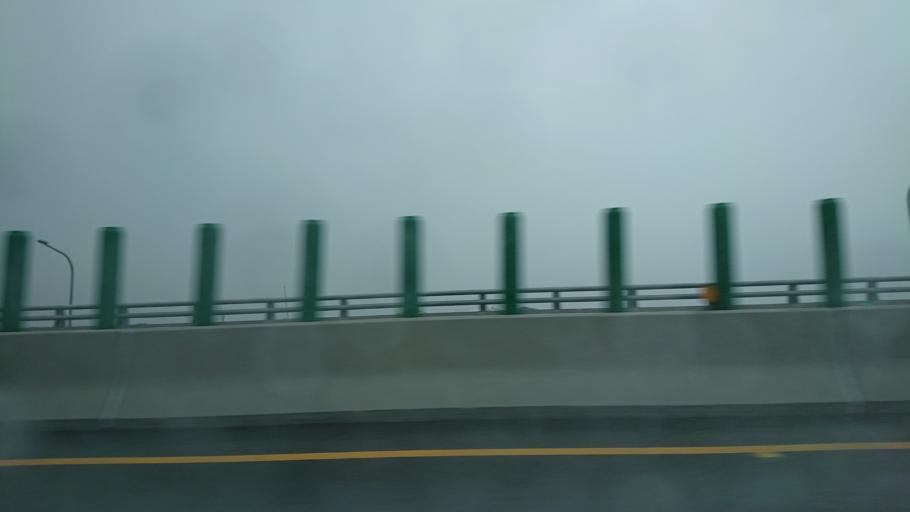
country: TW
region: Taiwan
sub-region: Changhua
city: Chang-hua
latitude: 23.9371
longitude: 120.3211
